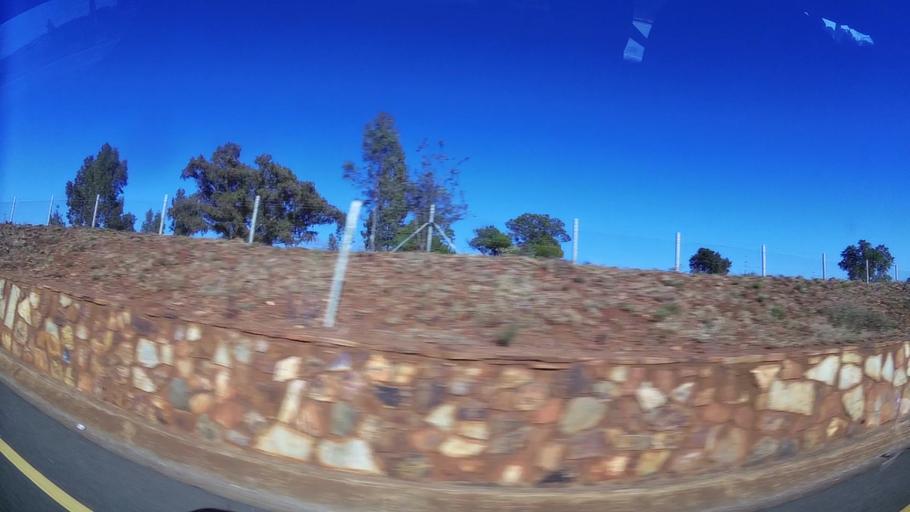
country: ZA
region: Gauteng
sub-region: City of Tshwane Metropolitan Municipality
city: Centurion
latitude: -25.8176
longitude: 28.2368
